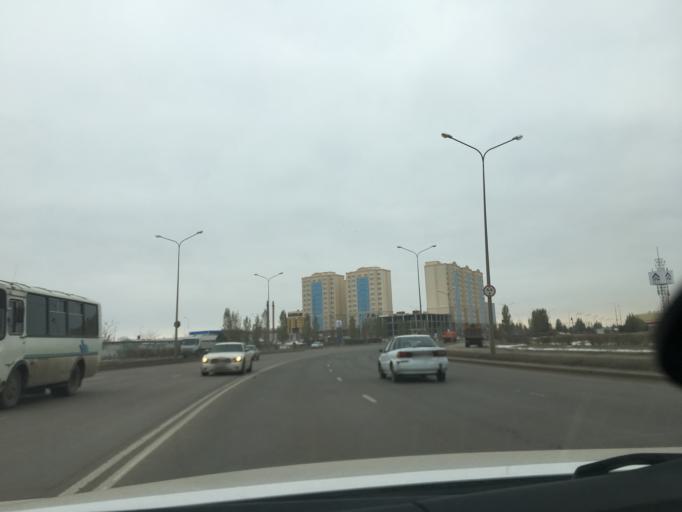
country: KZ
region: Astana Qalasy
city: Astana
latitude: 51.1473
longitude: 71.5300
